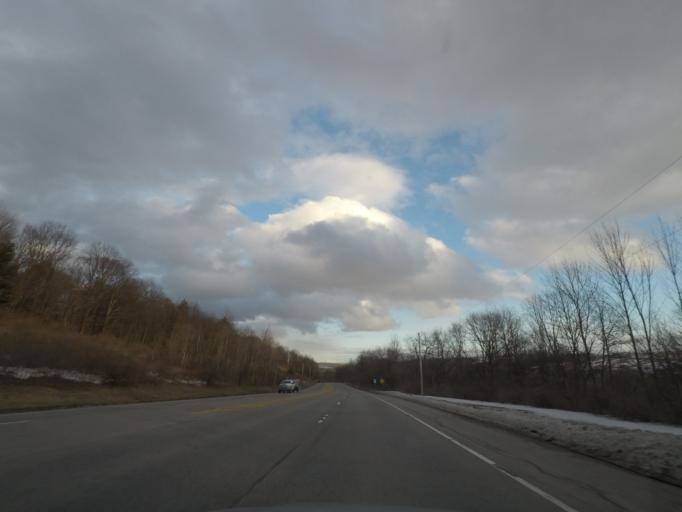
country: US
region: New York
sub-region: Montgomery County
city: Saint Johnsville
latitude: 43.0114
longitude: -74.7671
